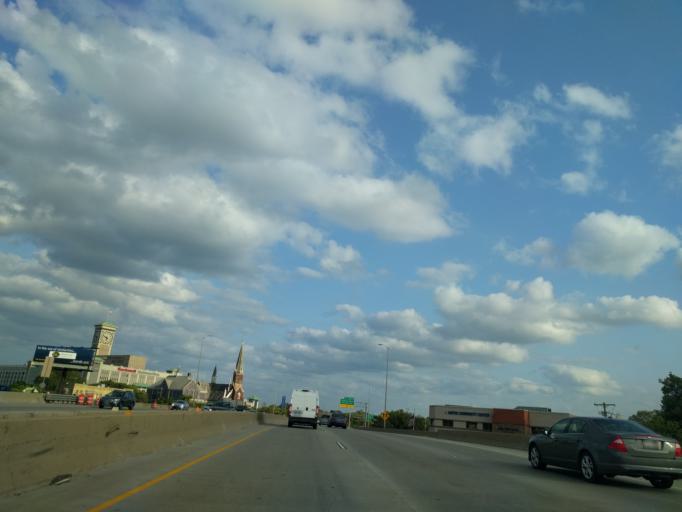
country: US
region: Wisconsin
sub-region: Milwaukee County
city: Milwaukee
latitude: 43.0209
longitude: -87.9195
